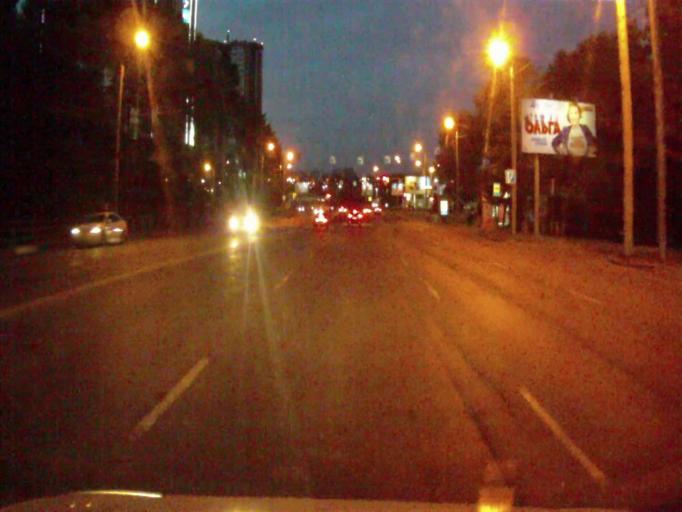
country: RU
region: Chelyabinsk
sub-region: Gorod Chelyabinsk
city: Chelyabinsk
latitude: 55.1660
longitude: 61.3808
